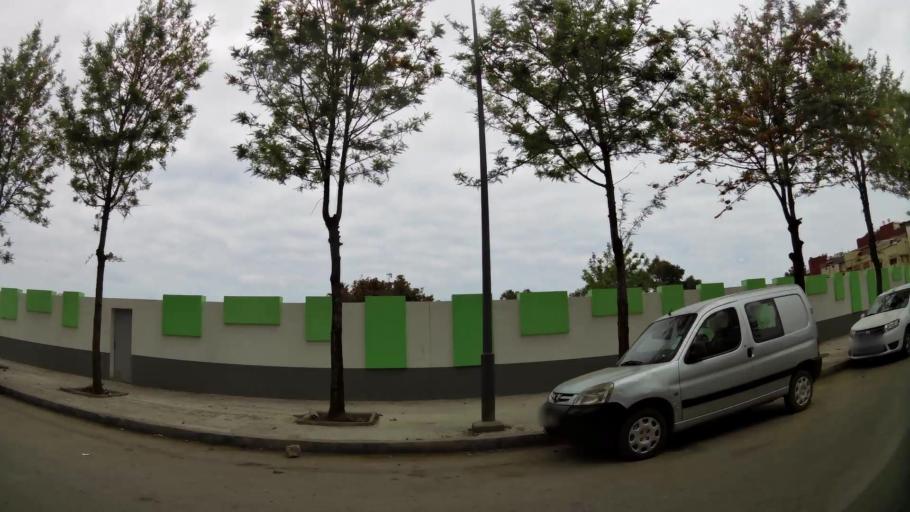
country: MA
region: Rabat-Sale-Zemmour-Zaer
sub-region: Rabat
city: Rabat
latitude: 33.9946
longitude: -6.8685
